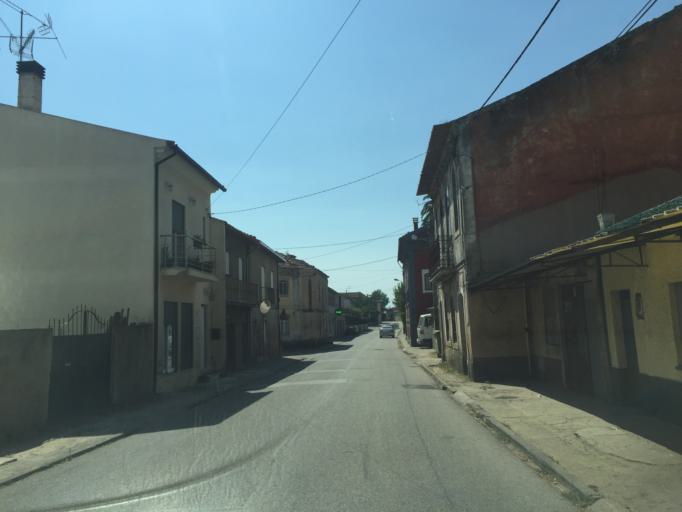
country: PT
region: Aveiro
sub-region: Mealhada
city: Mealhada
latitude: 40.3613
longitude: -8.5026
